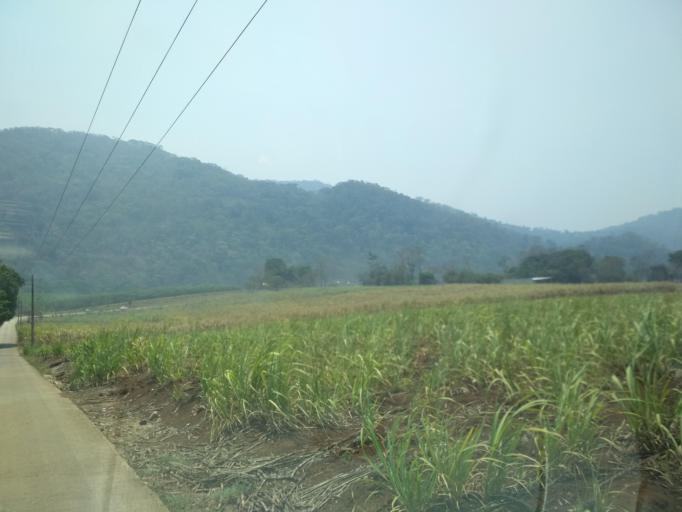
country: MX
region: Veracruz
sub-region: Tezonapa
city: Laguna Chica (Pueblo Nuevo)
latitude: 18.5689
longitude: -96.7230
